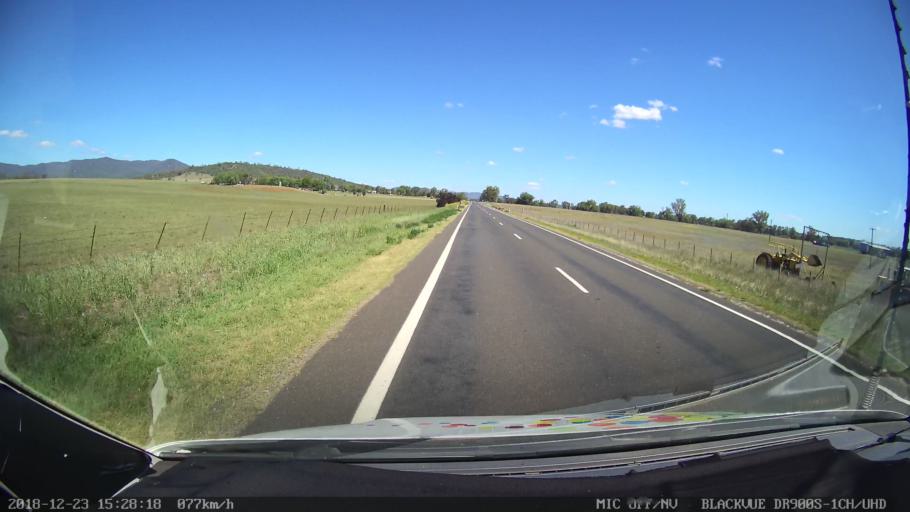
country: AU
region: New South Wales
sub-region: Tamworth Municipality
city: East Tamworth
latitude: -30.9349
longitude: 150.8512
